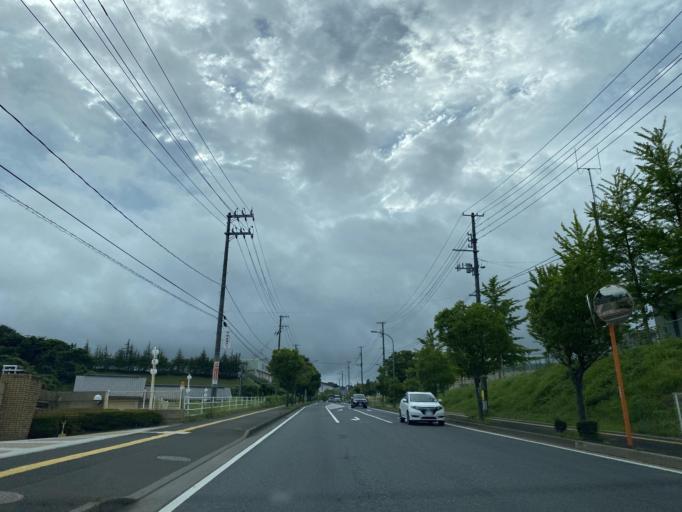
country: JP
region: Miyagi
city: Rifu
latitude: 38.3343
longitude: 140.9700
